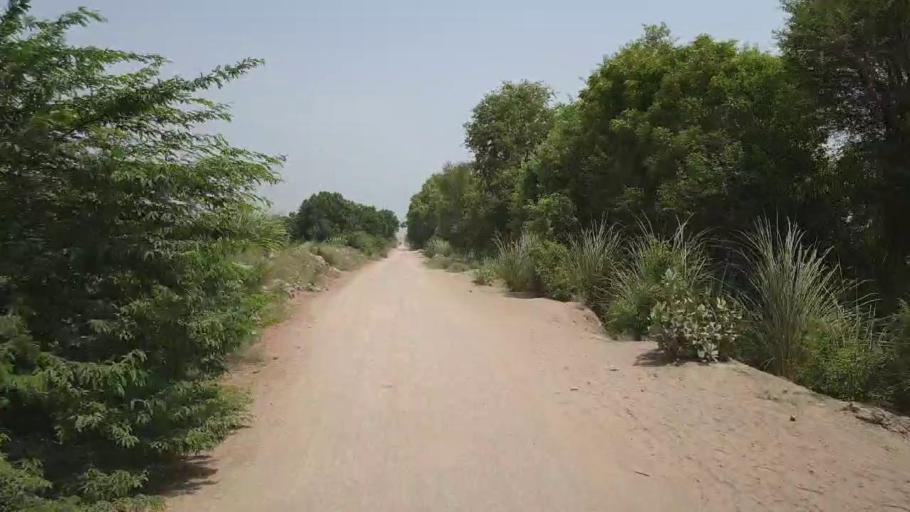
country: PK
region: Sindh
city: Nawabshah
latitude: 26.3141
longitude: 68.3003
